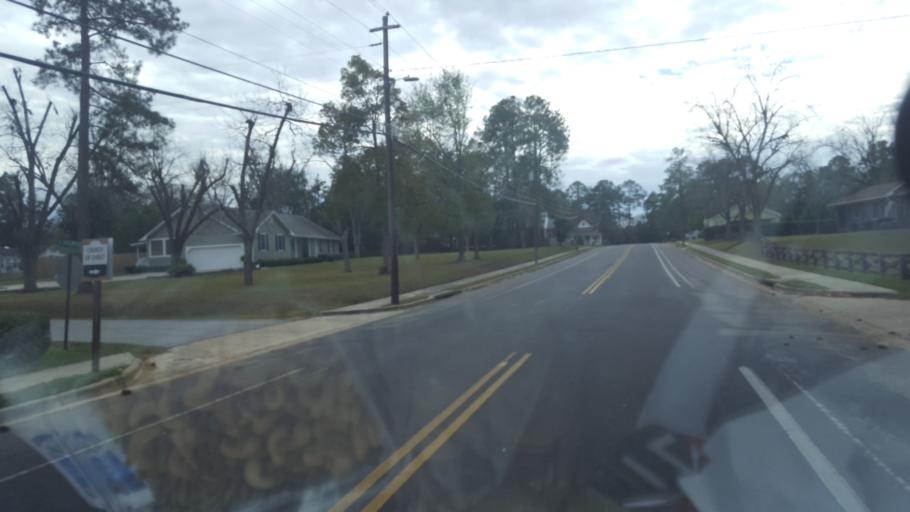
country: US
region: Georgia
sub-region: Berrien County
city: Nashville
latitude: 31.2053
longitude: -83.2548
